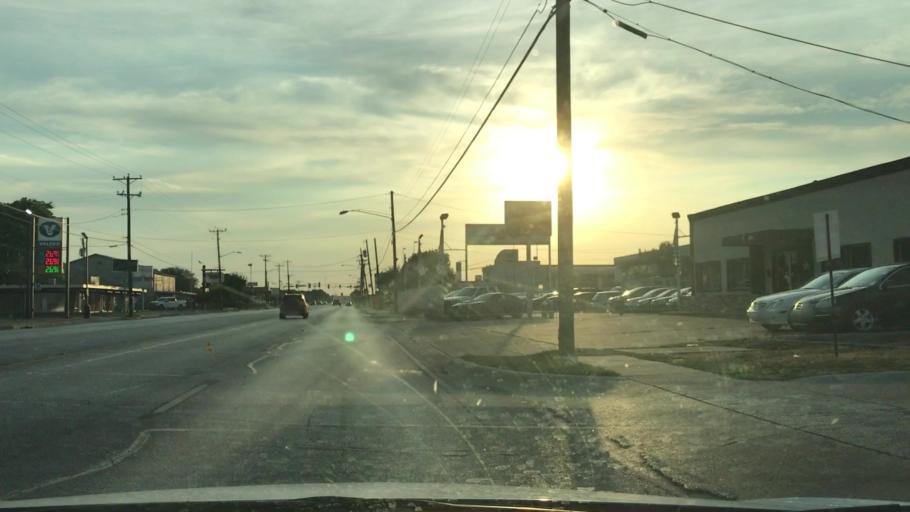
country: US
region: Texas
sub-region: Tarrant County
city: Haltom City
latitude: 32.7952
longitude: -97.3055
